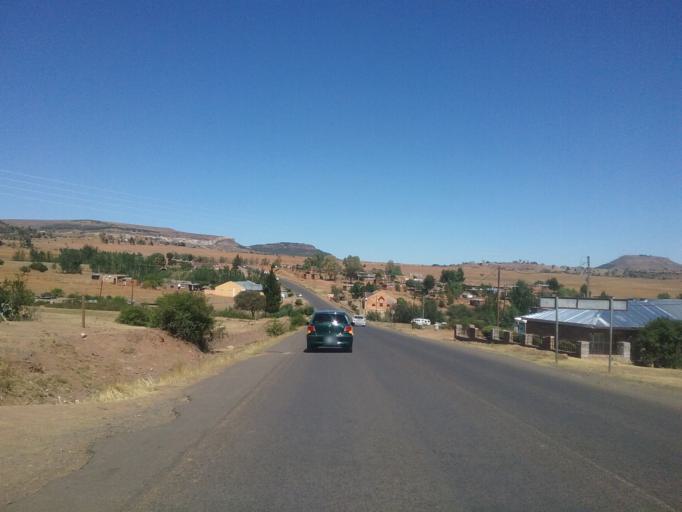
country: LS
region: Quthing
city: Quthing
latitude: -30.3975
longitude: 27.6640
